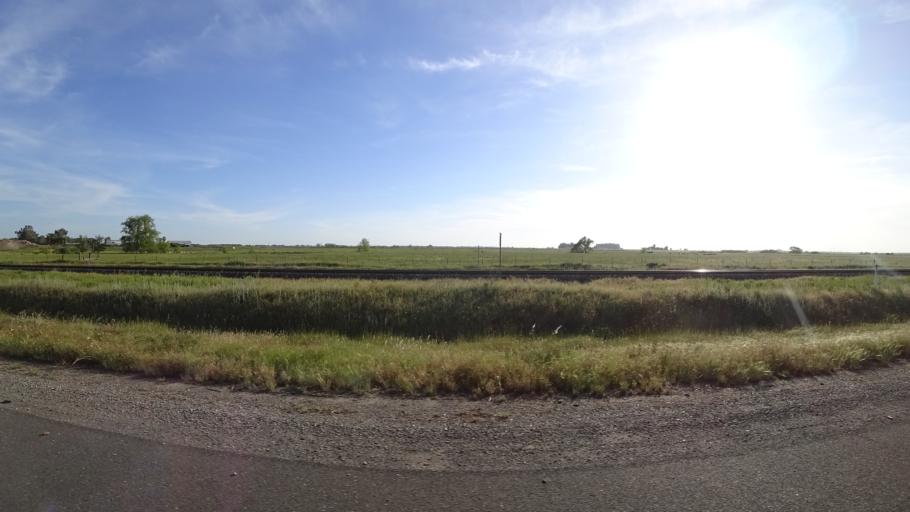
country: US
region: California
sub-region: Placer County
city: Sheridan
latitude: 38.9593
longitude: -121.3580
